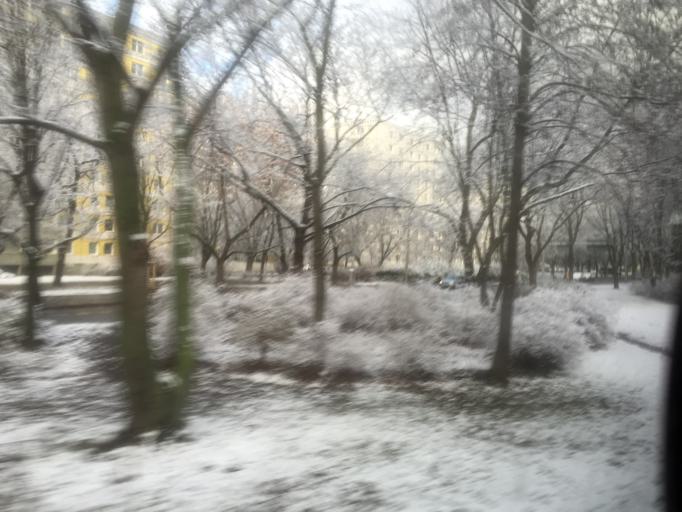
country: DE
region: Berlin
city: Berlin
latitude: 52.5141
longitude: 13.4252
